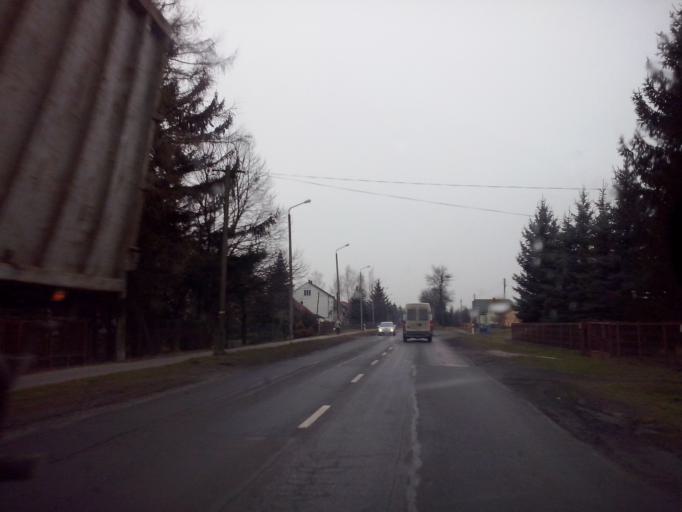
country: PL
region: Lublin Voivodeship
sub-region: Powiat zamojski
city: Szczebrzeszyn
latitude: 50.7055
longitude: 22.9960
